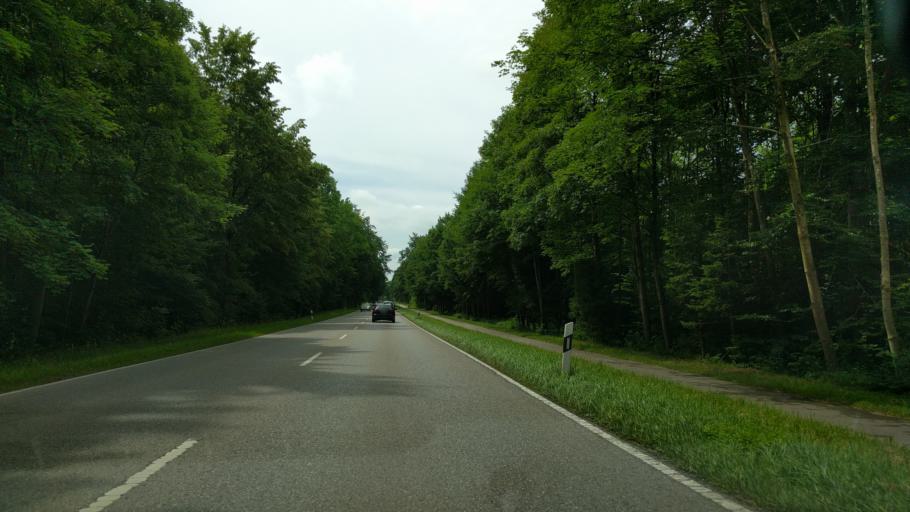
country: DE
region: Bavaria
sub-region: Upper Bavaria
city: Strasslach-Dingharting
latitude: 48.0198
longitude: 11.5174
